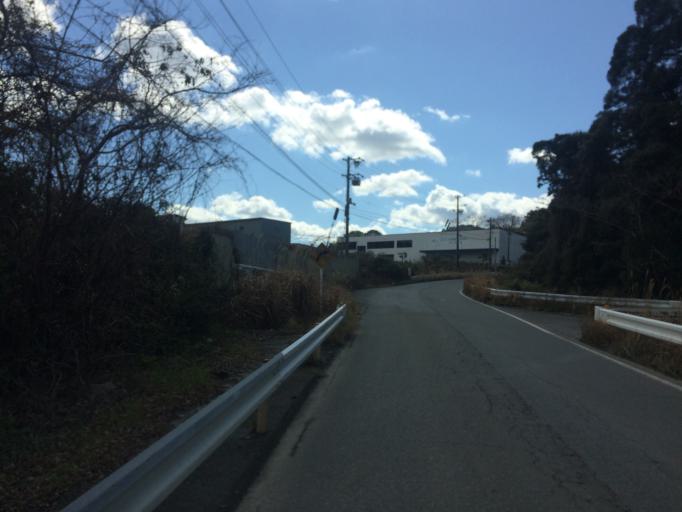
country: JP
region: Shizuoka
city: Shimada
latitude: 34.7730
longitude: 138.1990
